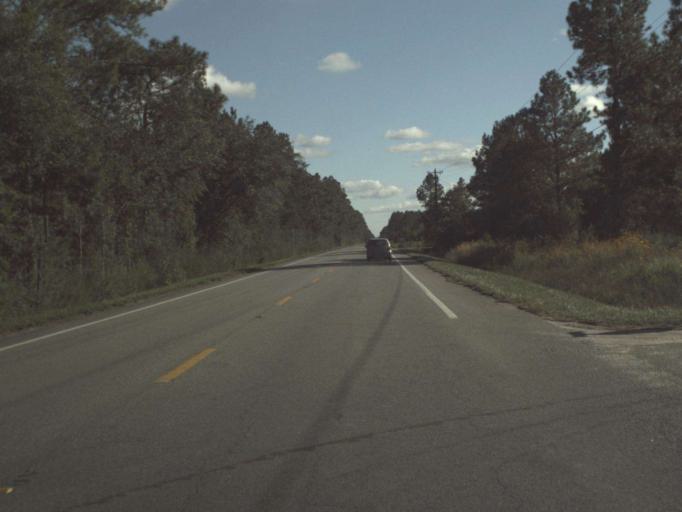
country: US
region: Florida
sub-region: Gulf County
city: Wewahitchka
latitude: 30.0348
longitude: -85.1828
